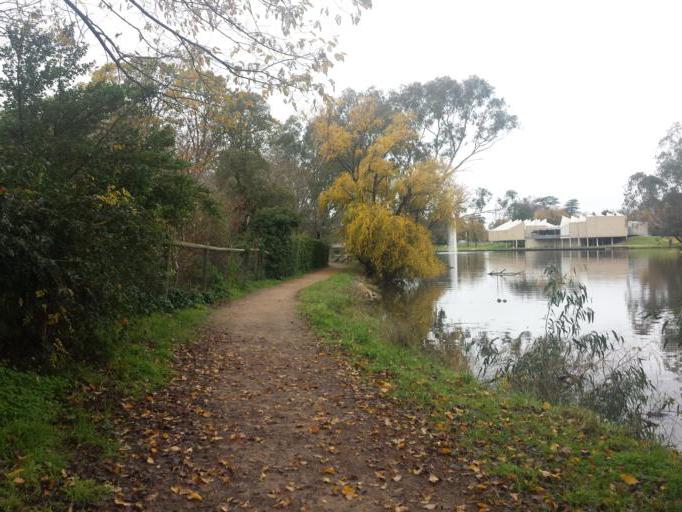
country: AU
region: Victoria
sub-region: Benalla
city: Benalla
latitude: -36.5499
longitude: 145.9789
